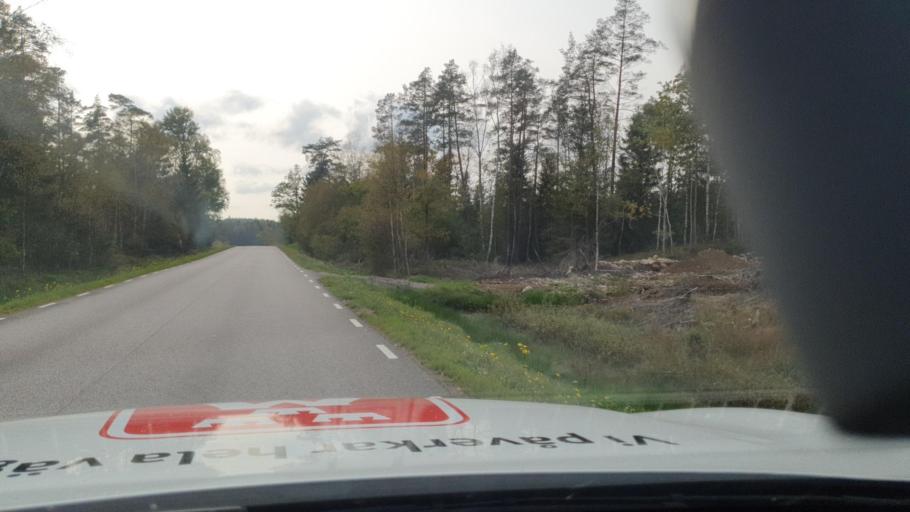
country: SE
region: Halland
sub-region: Hylte Kommun
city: Hyltebruk
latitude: 56.7802
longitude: 13.2348
